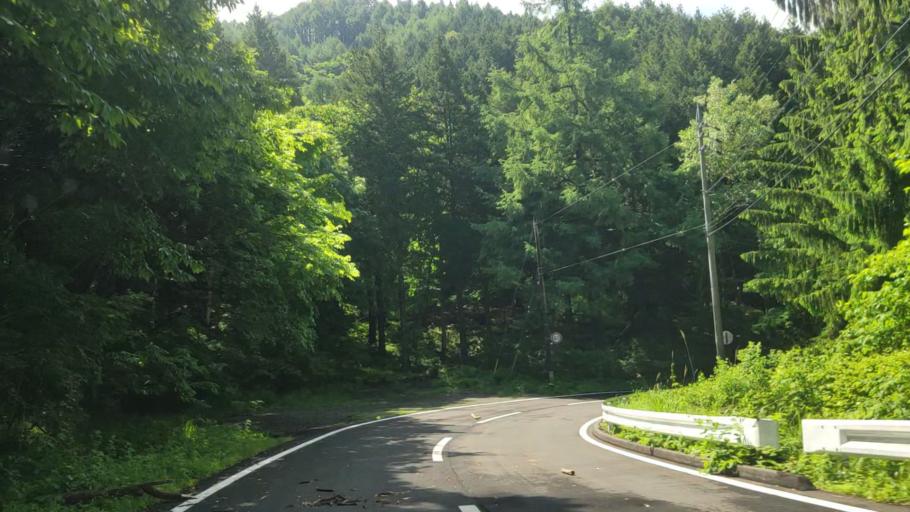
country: JP
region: Nagano
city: Suwa
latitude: 36.0791
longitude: 138.1390
